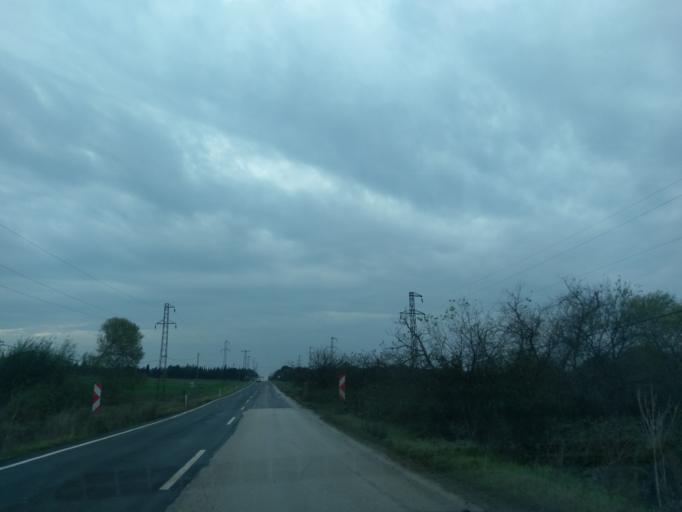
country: TR
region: Istanbul
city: Canta
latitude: 41.1428
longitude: 28.1069
